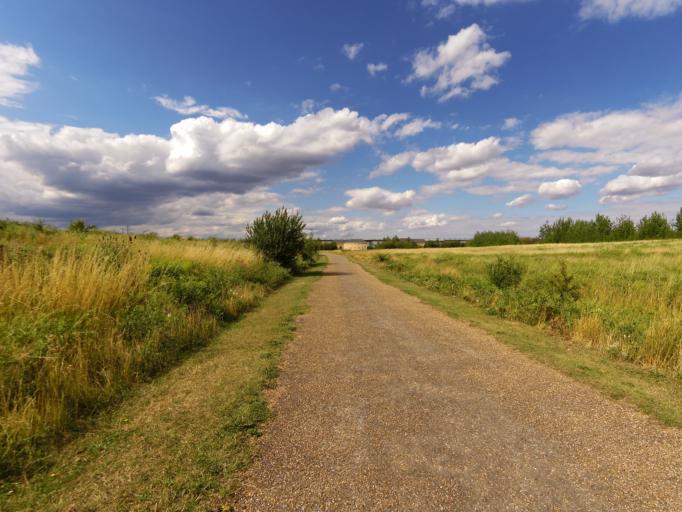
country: GB
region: England
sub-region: Essex
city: Waltham Abbey
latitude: 51.6744
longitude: -0.0051
